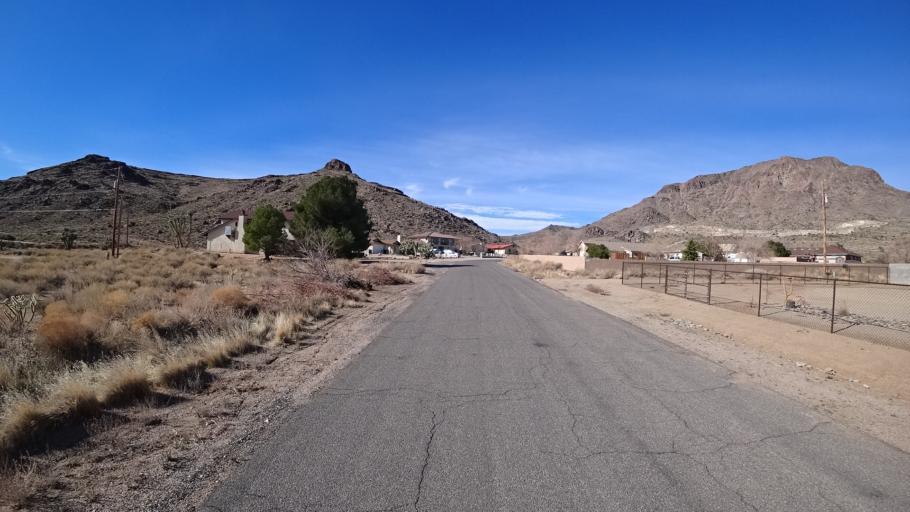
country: US
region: Arizona
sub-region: Mohave County
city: New Kingman-Butler
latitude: 35.2672
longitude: -114.0491
